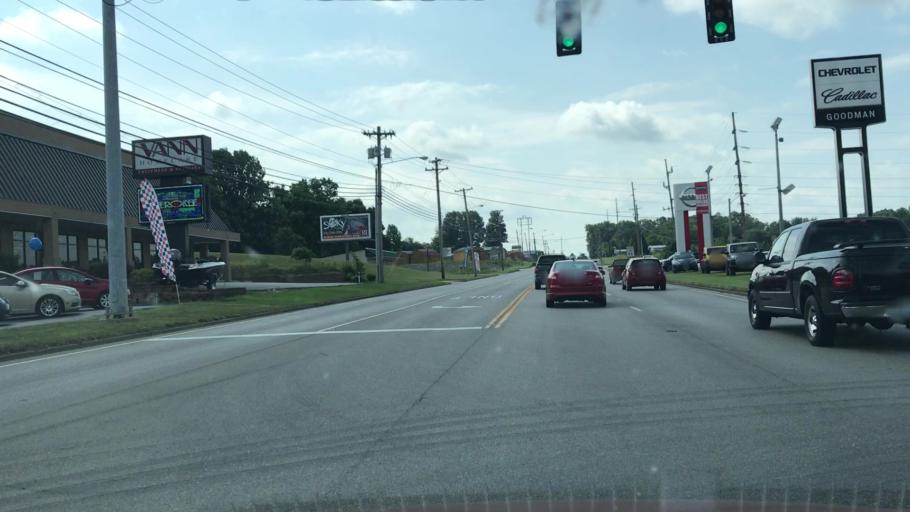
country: US
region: Kentucky
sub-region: Barren County
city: Glasgow
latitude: 37.0152
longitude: -85.9278
